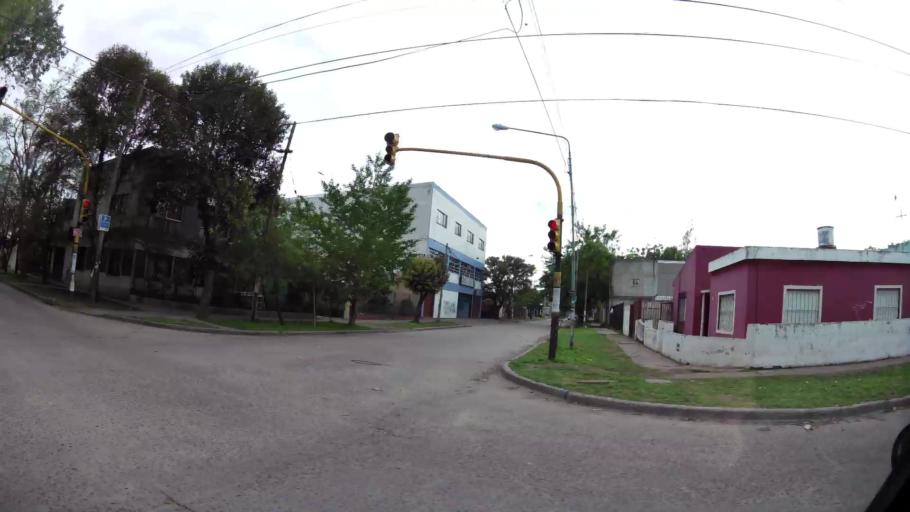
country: AR
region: Buenos Aires
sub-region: Partido de Quilmes
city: Quilmes
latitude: -34.8025
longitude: -58.2716
